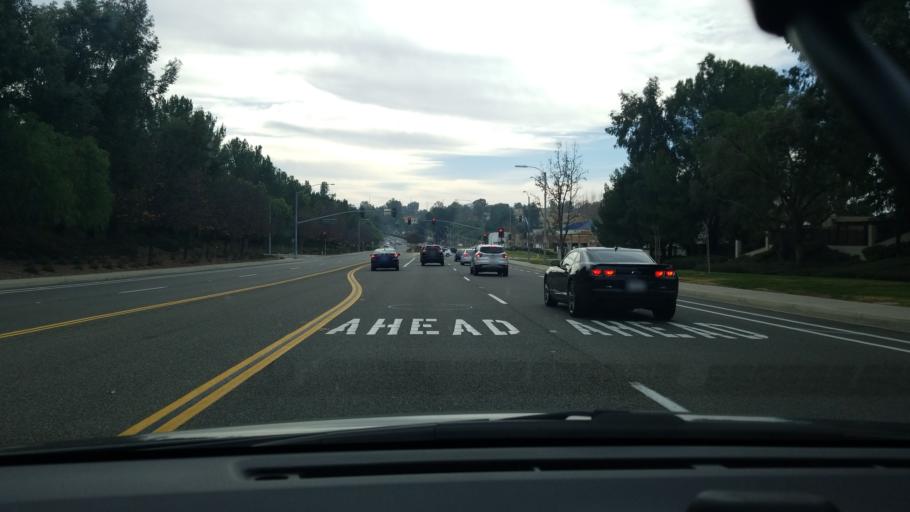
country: US
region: California
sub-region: Riverside County
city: Temecula
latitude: 33.5113
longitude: -117.1239
